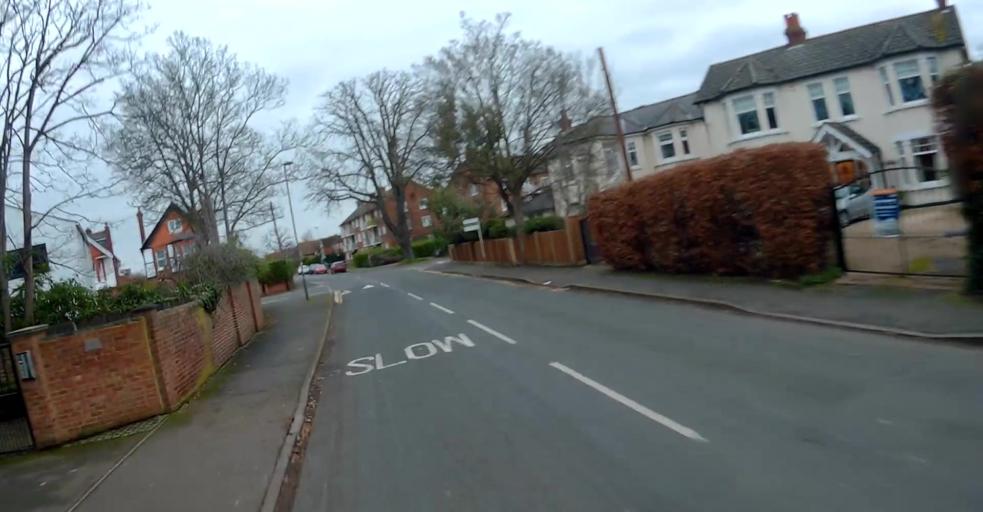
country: GB
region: England
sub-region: Surrey
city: Walton-on-Thames
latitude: 51.3821
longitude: -0.4071
